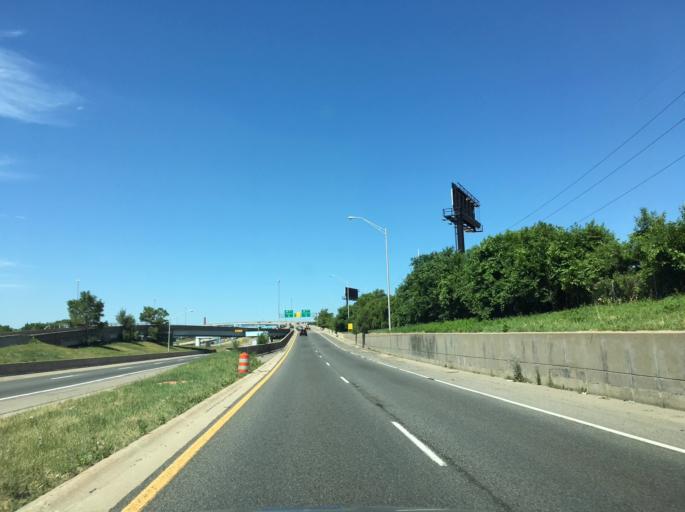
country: US
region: Michigan
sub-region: Wayne County
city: Dearborn
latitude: 42.3794
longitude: -83.2089
